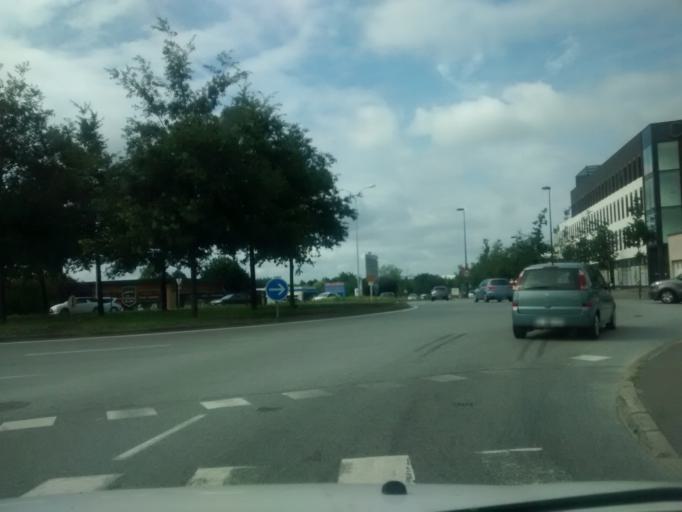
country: FR
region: Brittany
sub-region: Departement d'Ille-et-Vilaine
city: Saint-Jacques-de-la-Lande
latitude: 48.0871
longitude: -1.7074
